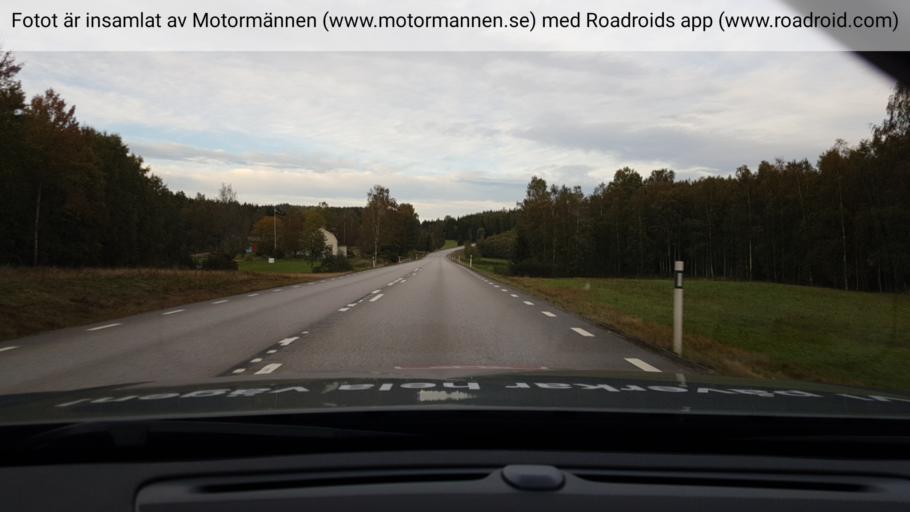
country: SE
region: Vaestra Goetaland
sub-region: Bengtsfors Kommun
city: Dals Langed
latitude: 59.0241
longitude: 12.3834
